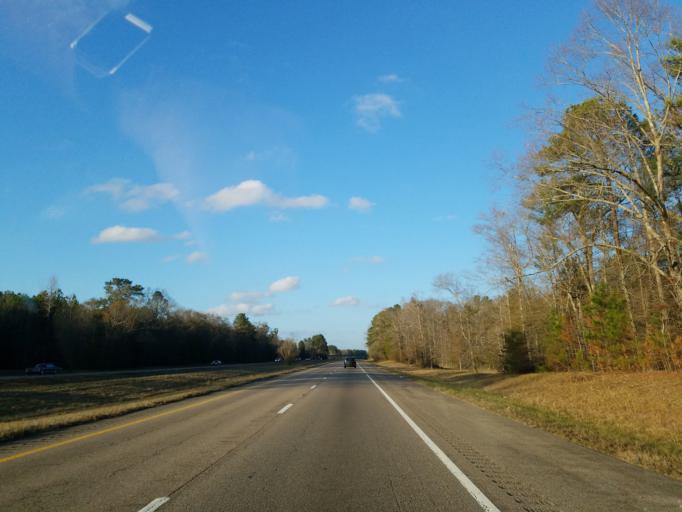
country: US
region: Mississippi
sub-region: Clarke County
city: Stonewall
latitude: 32.0319
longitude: -88.9218
